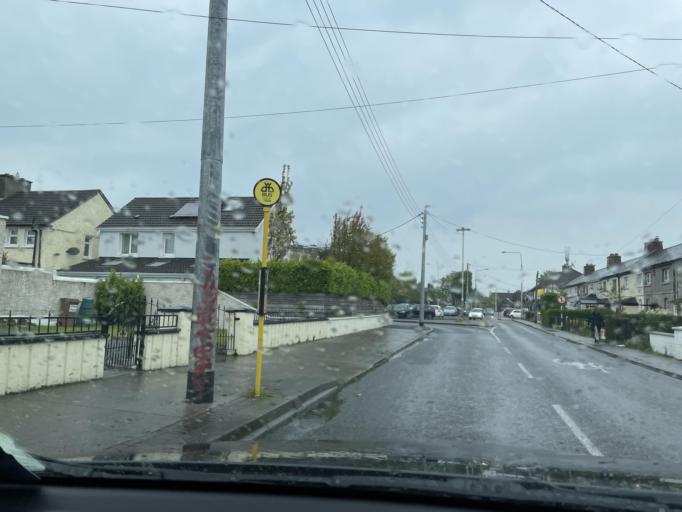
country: IE
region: Leinster
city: Dundrum
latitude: 53.2939
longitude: -6.2573
